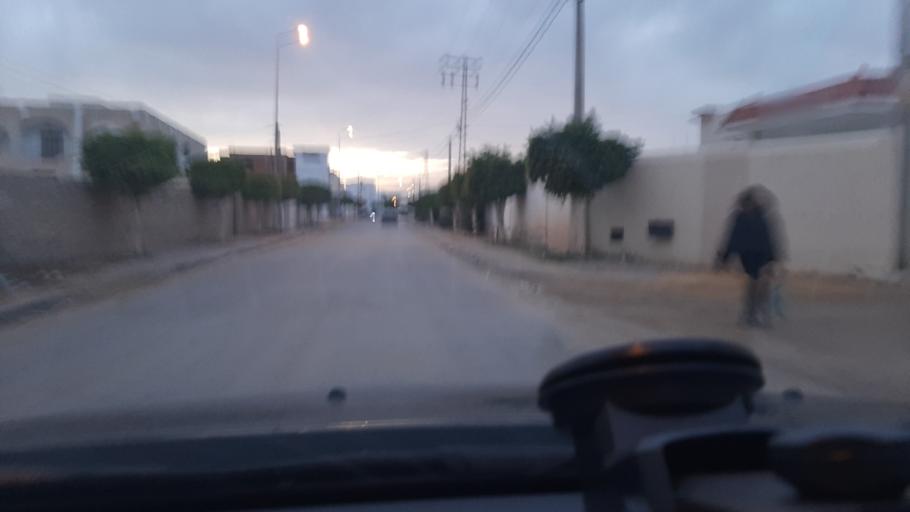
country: TN
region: Safaqis
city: Sfax
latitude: 34.7672
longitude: 10.7014
